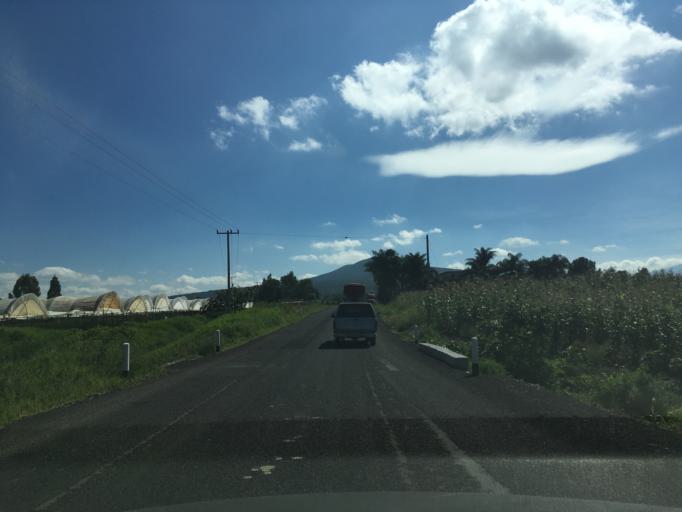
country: MX
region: Mexico
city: Tlazazalca
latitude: 19.9724
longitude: -102.0699
